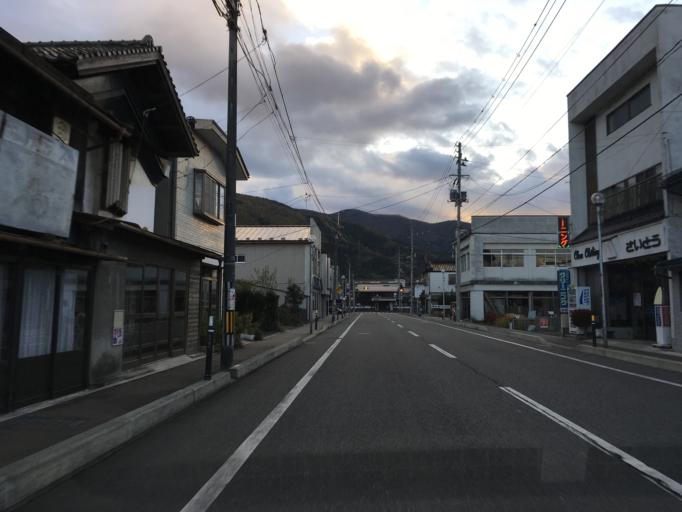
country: JP
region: Iwate
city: Tono
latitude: 39.3295
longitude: 141.5255
